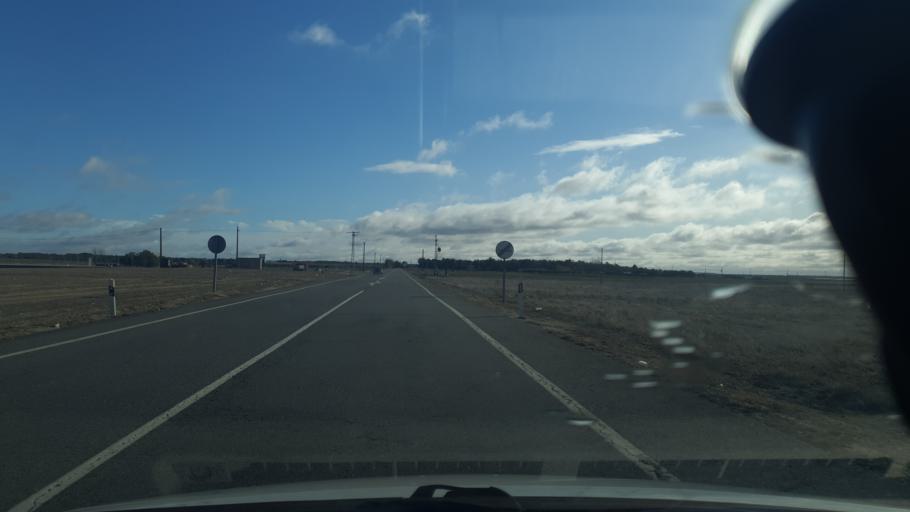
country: ES
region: Castille and Leon
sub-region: Provincia de Segovia
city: Martin Munoz de la Dehesa
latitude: 41.0480
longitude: -4.6927
